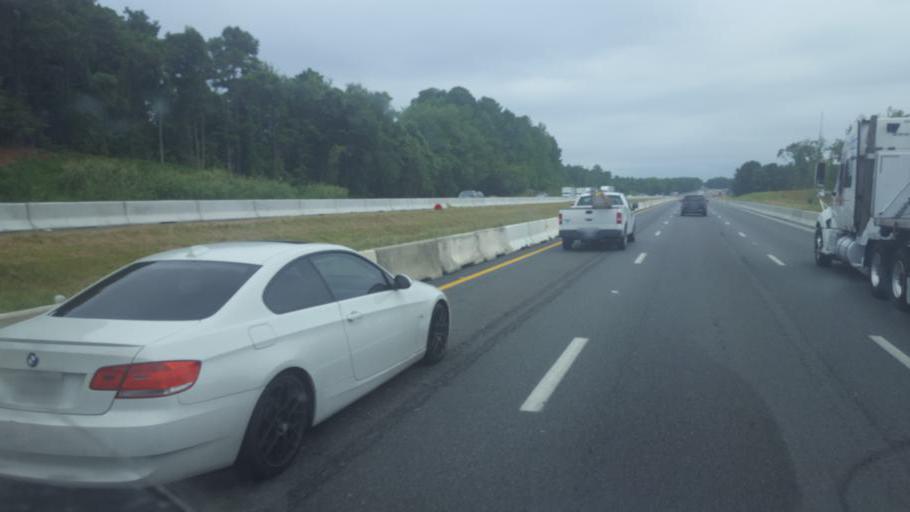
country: US
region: North Carolina
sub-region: Mecklenburg County
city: Huntersville
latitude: 35.3344
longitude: -80.8485
